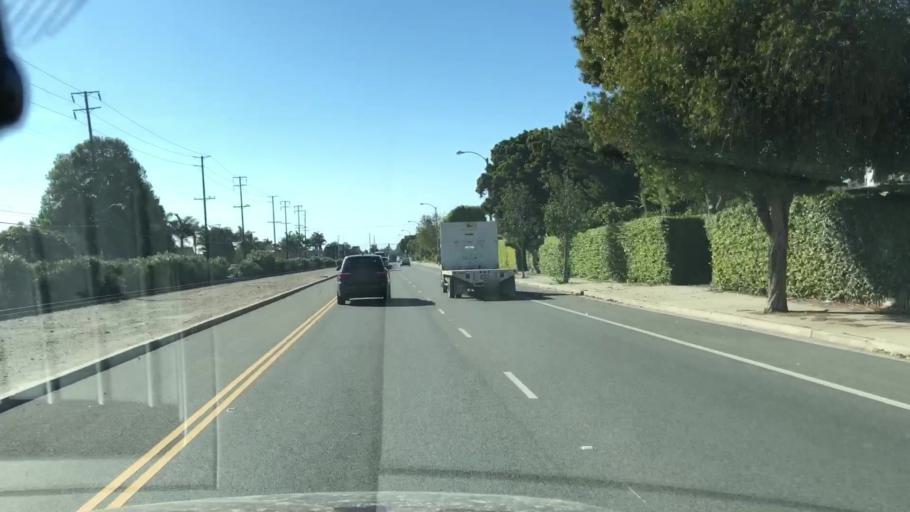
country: US
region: California
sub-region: Ventura County
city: Oxnard
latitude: 34.1903
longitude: -119.1912
